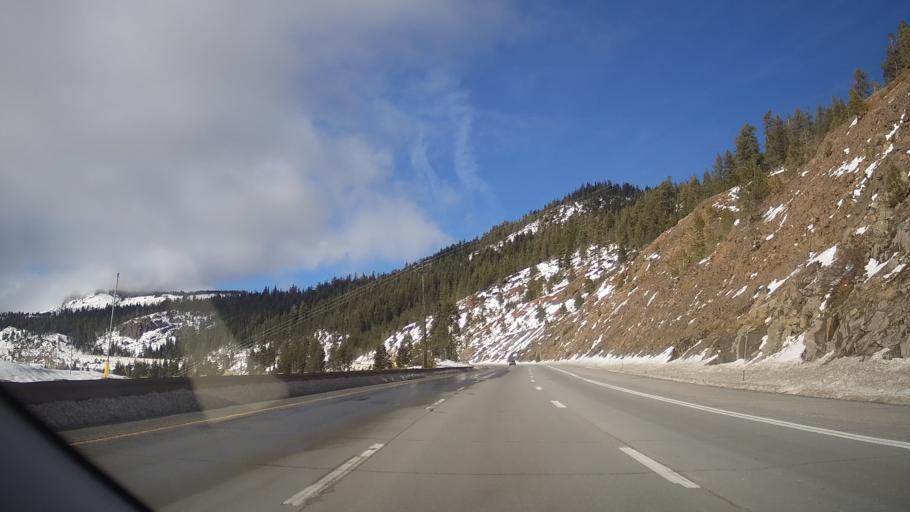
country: US
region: California
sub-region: Nevada County
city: Truckee
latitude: 39.3349
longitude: -120.3054
